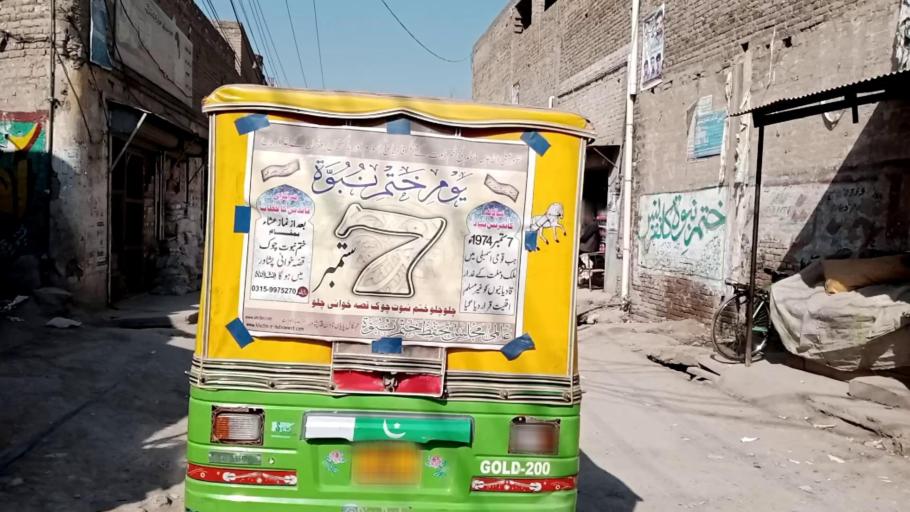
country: PK
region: Khyber Pakhtunkhwa
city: Peshawar
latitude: 34.0107
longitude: 71.5167
